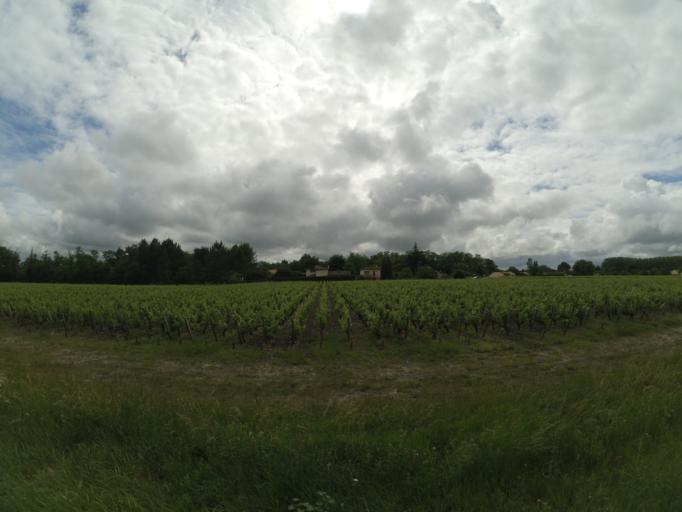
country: FR
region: Aquitaine
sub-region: Departement de la Gironde
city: Soussans
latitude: 45.0535
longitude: -0.6958
